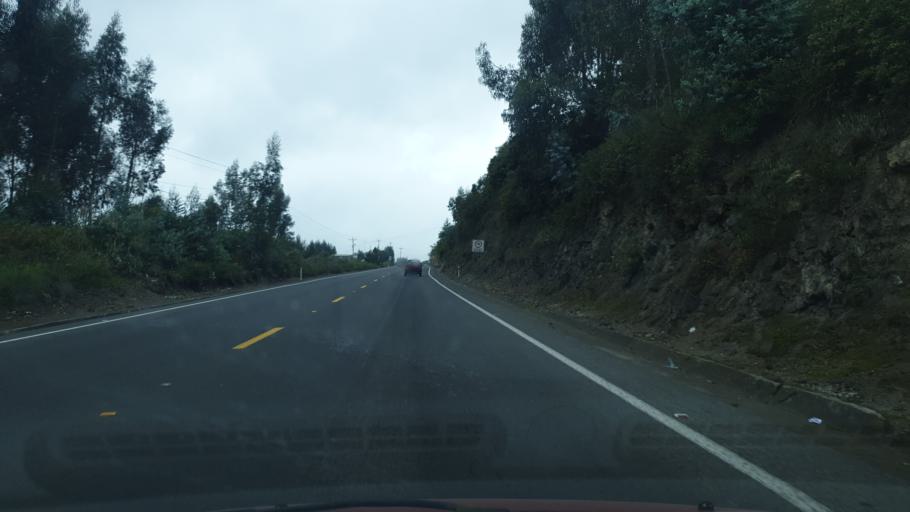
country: EC
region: Tungurahua
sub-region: Canton Quero
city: Quero
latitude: -1.3803
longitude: -78.6487
